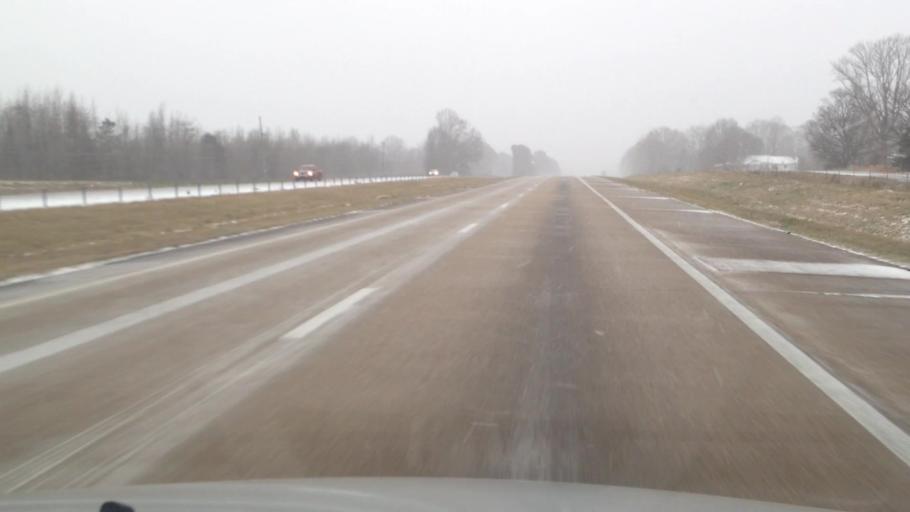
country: US
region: Mississippi
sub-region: Hinds County
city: Edwards
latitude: 32.3506
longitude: -90.5646
